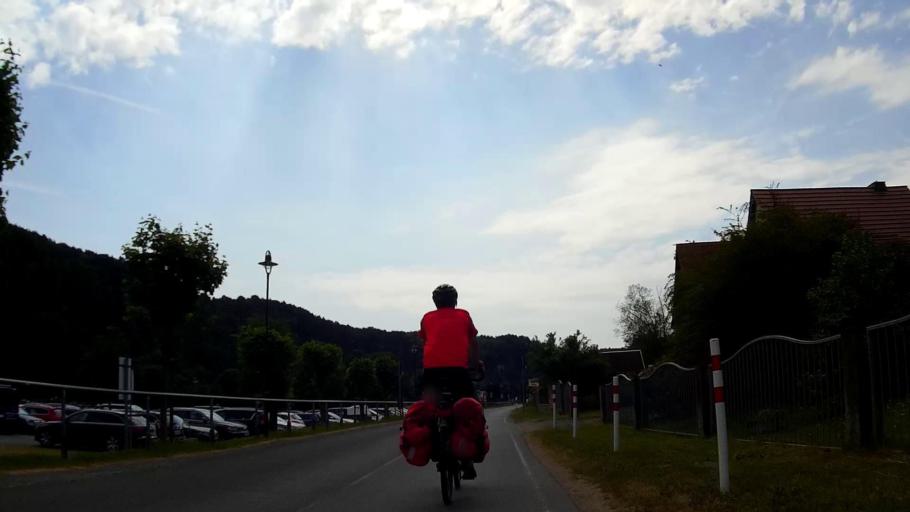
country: DE
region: Saxony
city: Konigstein
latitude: 50.9559
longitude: 14.0792
